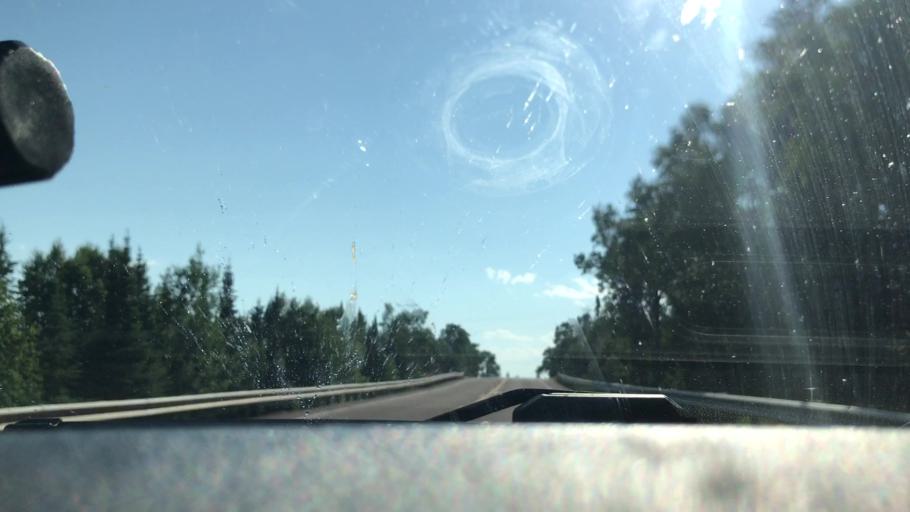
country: US
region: Minnesota
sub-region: Cook County
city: Grand Marais
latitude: 47.8300
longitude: -89.9862
